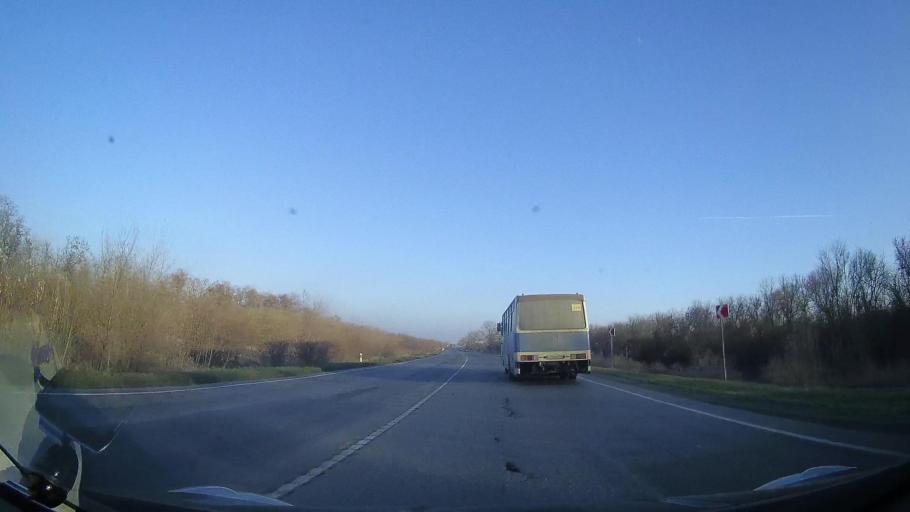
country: RU
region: Rostov
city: Kirovskaya
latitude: 47.0167
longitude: 39.9078
